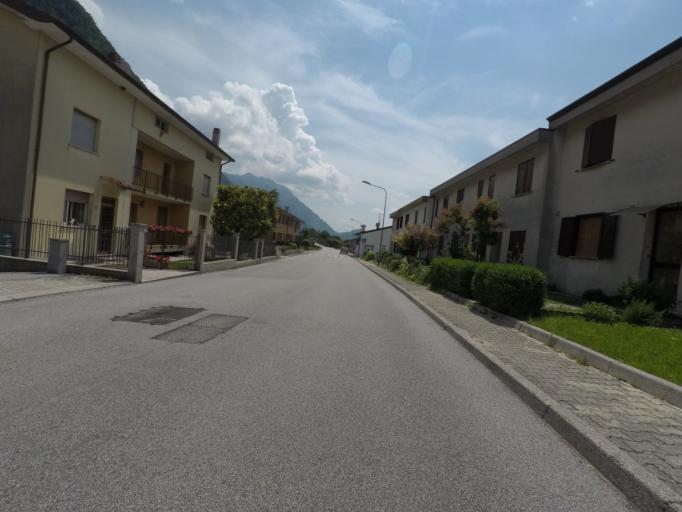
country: IT
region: Friuli Venezia Giulia
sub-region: Provincia di Udine
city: Venzone
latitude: 46.3695
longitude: 13.1336
